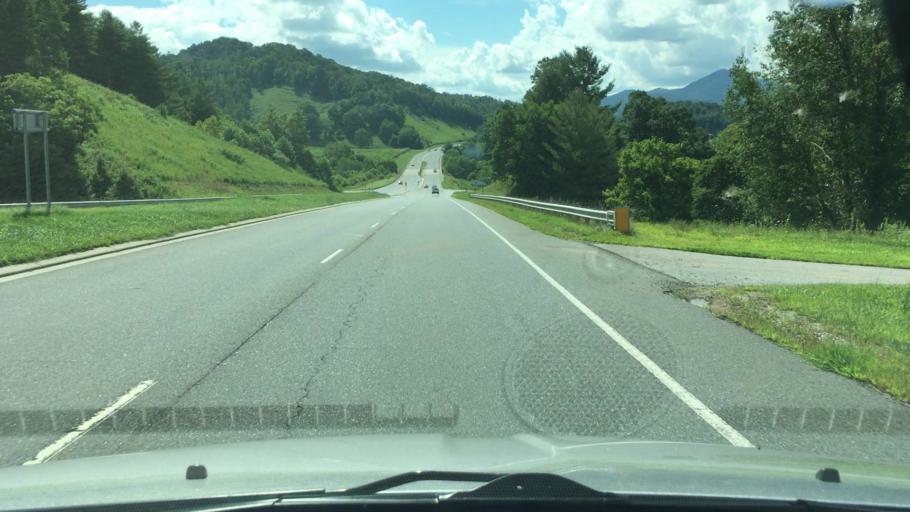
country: US
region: North Carolina
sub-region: Yancey County
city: Burnsville
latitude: 35.9109
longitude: -82.3772
